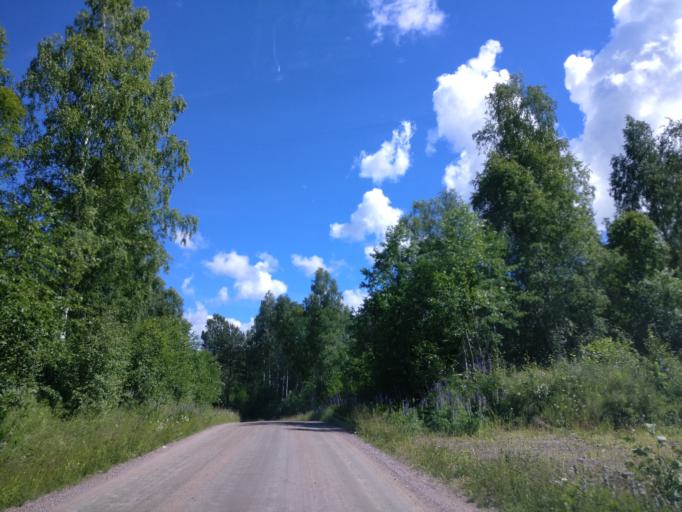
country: SE
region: Vaermland
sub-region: Hagfors Kommun
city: Hagfors
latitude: 60.0405
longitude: 13.6508
